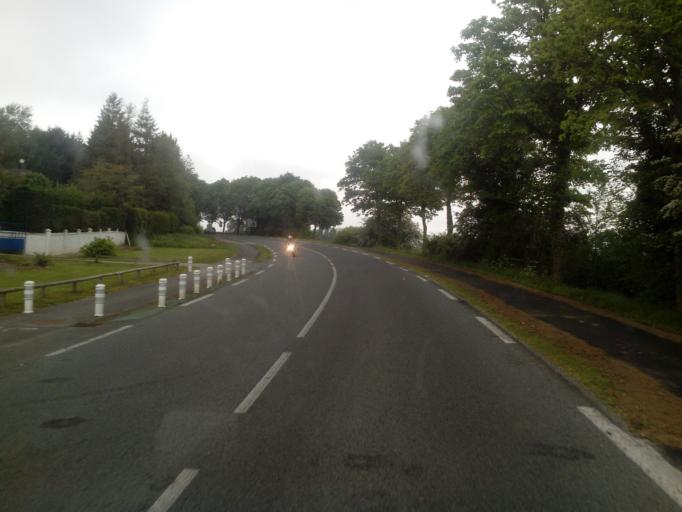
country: FR
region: Nord-Pas-de-Calais
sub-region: Departement du Pas-de-Calais
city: Condette
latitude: 50.6633
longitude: 1.6416
